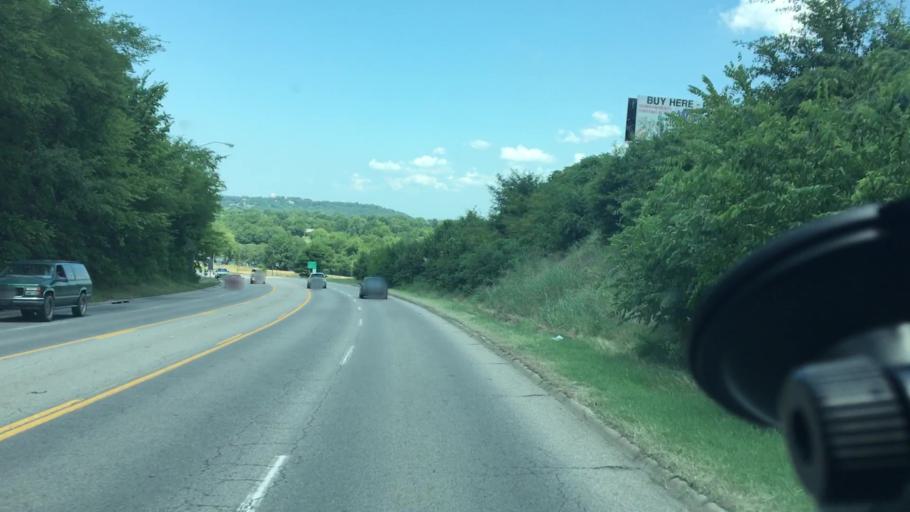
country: US
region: Arkansas
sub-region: Sebastian County
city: Barling
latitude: 35.3395
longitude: -94.3201
